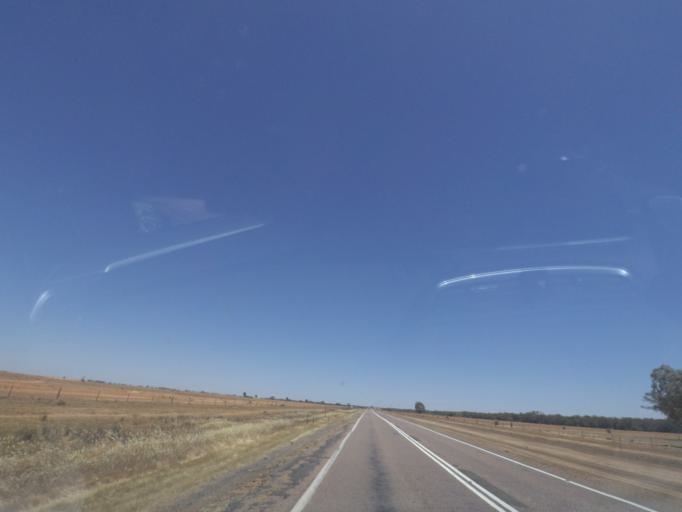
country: AU
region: New South Wales
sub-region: Berrigan
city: Berrigan
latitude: -35.1495
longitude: 145.9998
